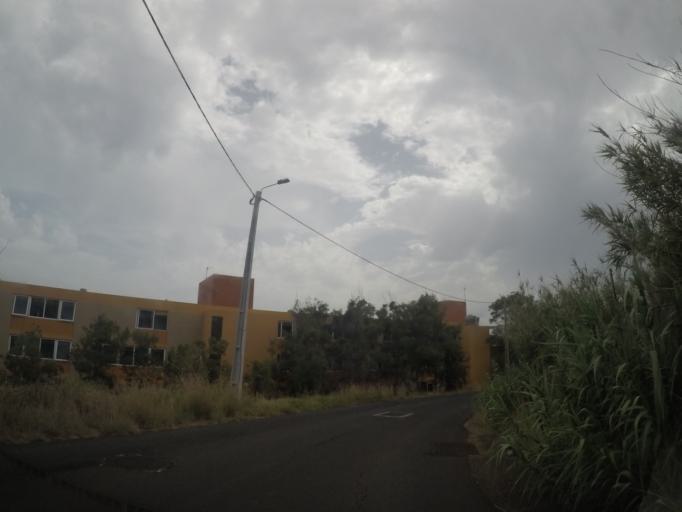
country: PT
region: Madeira
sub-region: Santa Cruz
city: Santa Cruz
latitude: 32.6525
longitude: -16.8189
